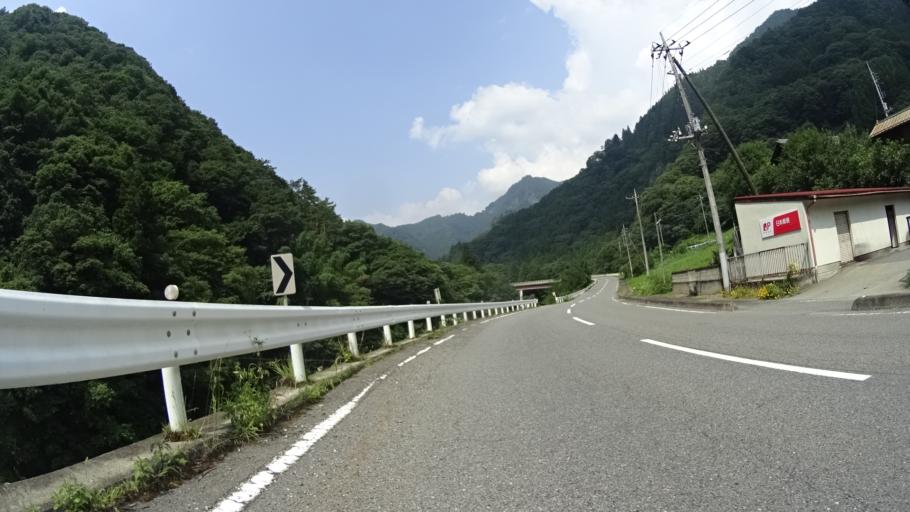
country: JP
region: Gunma
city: Tomioka
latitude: 36.0915
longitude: 138.8128
